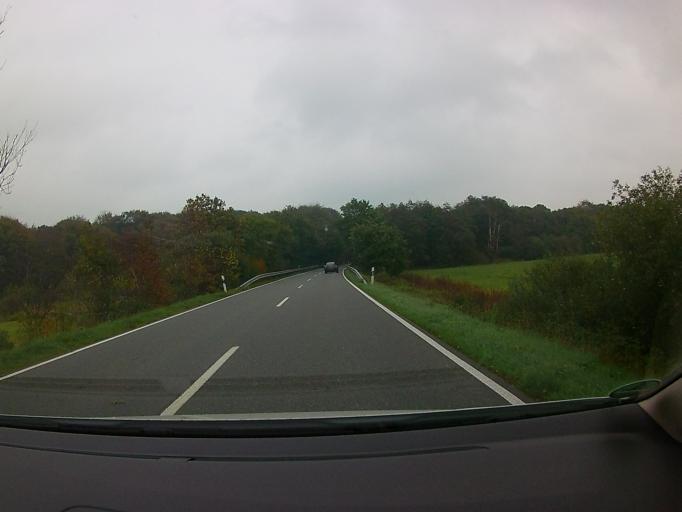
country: DE
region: Schleswig-Holstein
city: Lindewitt
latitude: 54.6921
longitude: 9.2126
